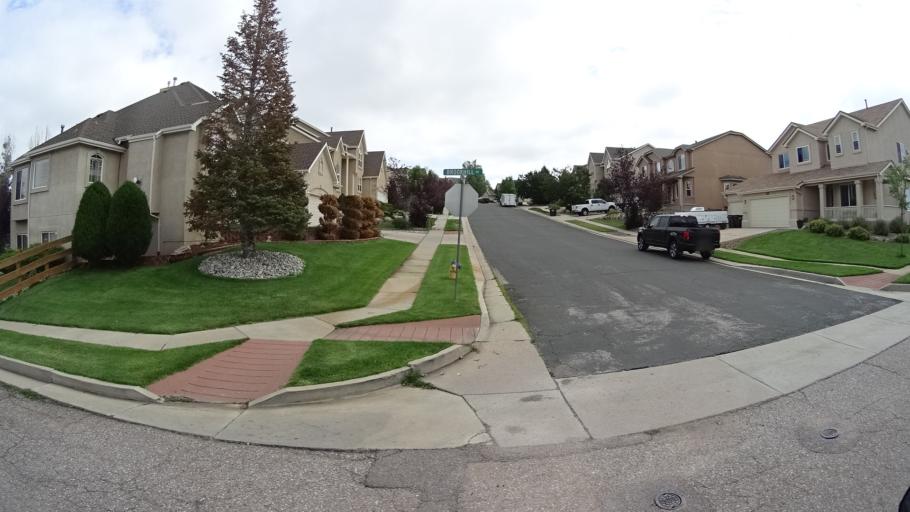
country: US
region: Colorado
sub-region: El Paso County
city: Gleneagle
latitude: 39.0154
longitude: -104.8062
